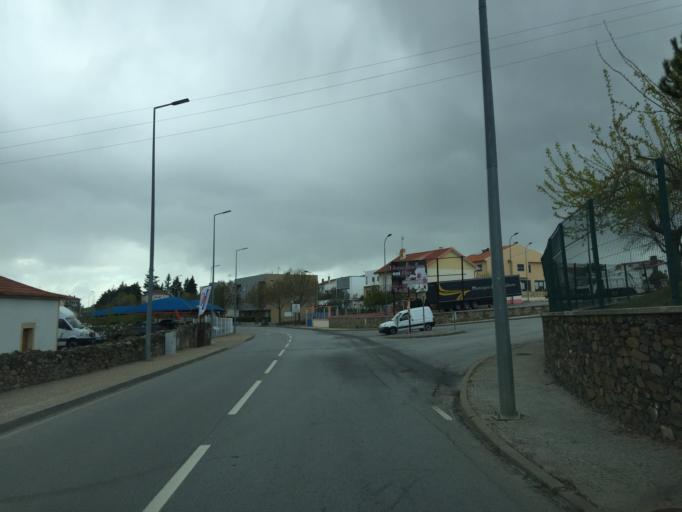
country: PT
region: Braganca
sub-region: Mogadouro
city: Mogadouro
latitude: 41.3423
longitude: -6.7042
